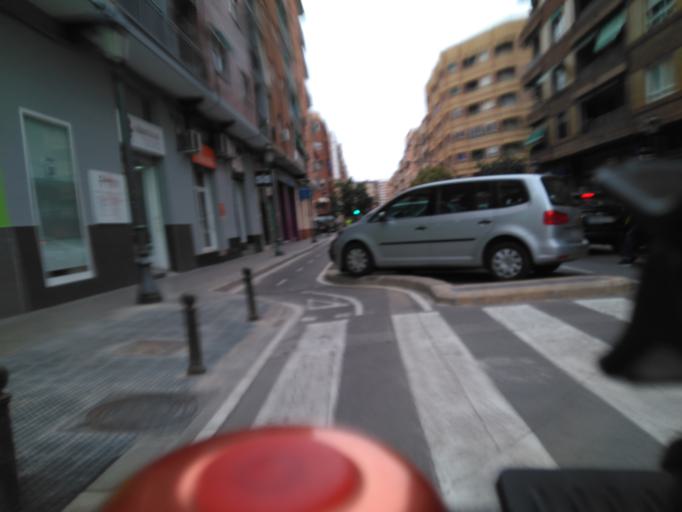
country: ES
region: Valencia
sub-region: Provincia de Valencia
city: Mislata
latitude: 39.4714
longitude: -0.3990
